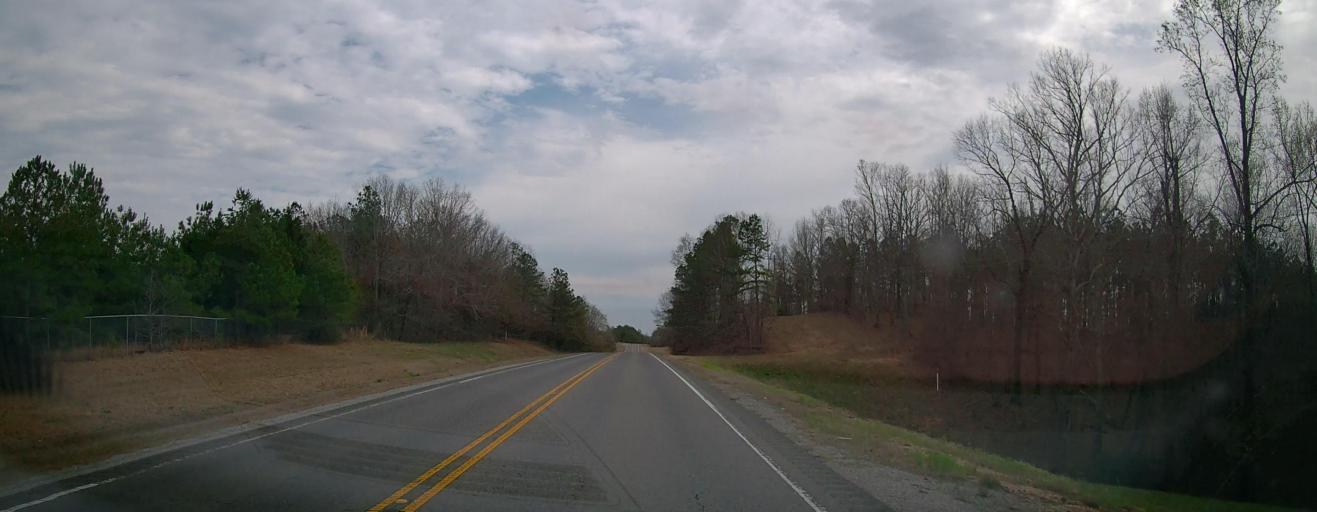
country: US
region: Alabama
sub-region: Marion County
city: Guin
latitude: 34.0335
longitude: -87.9463
